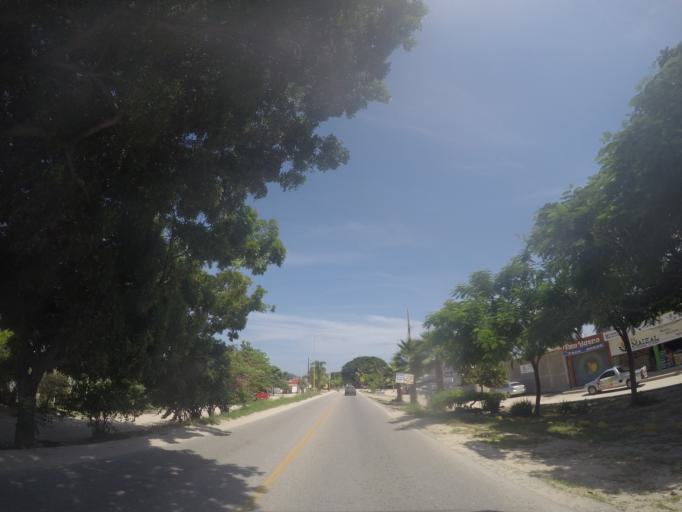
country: MX
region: Oaxaca
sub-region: Villa de Tututepec de Melchor Ocampo
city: Santa Rosa de Lima
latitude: 16.0085
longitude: -97.4339
